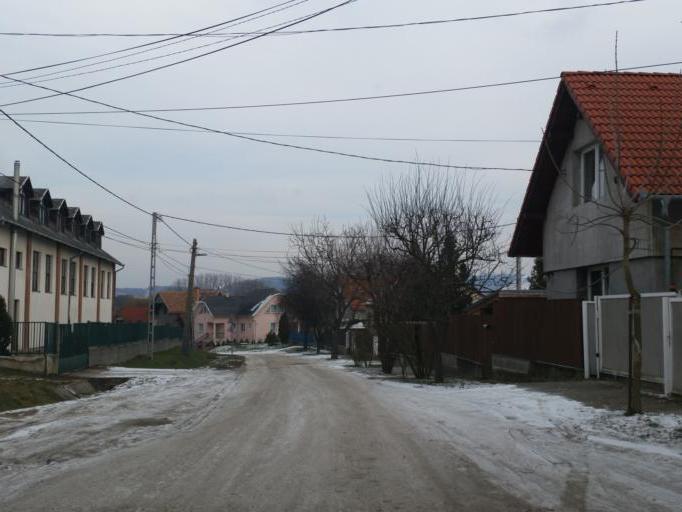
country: HU
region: Pest
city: Perbal
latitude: 47.5905
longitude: 18.7634
